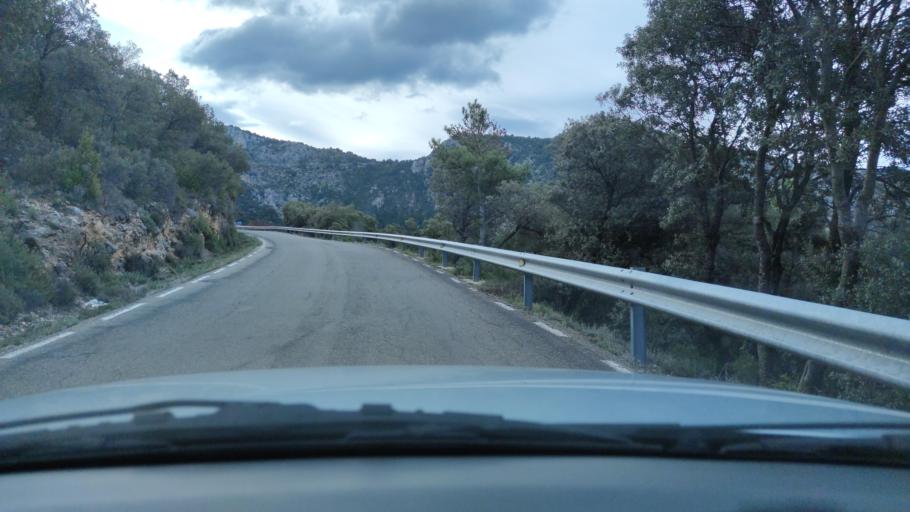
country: ES
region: Catalonia
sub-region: Provincia de Lleida
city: Coll de Nargo
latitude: 42.2476
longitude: 1.3566
